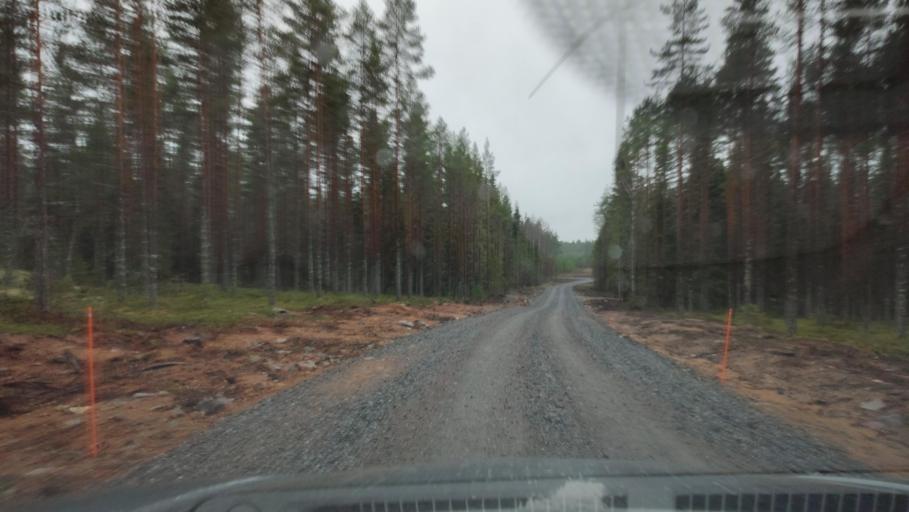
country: FI
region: Southern Ostrobothnia
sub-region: Suupohja
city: Karijoki
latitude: 62.1567
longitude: 21.6119
